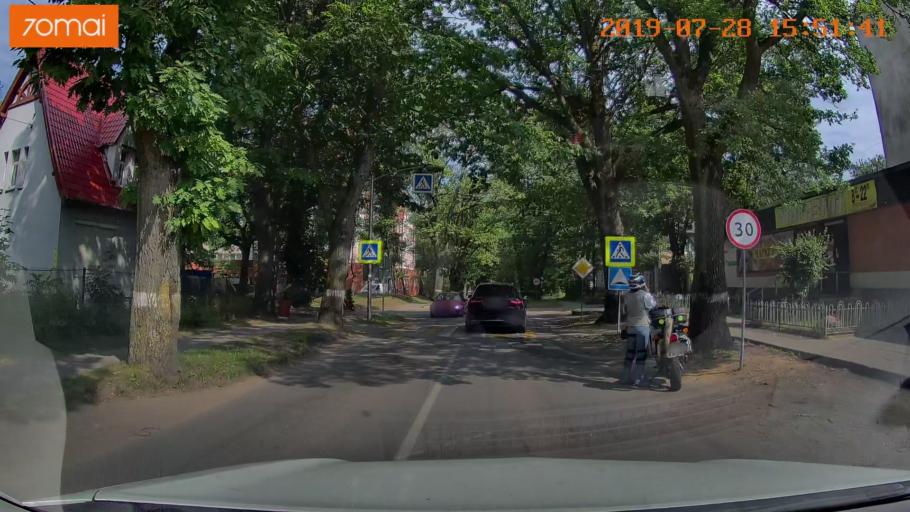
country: RU
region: Kaliningrad
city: Otradnoye
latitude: 54.9411
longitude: 20.1074
